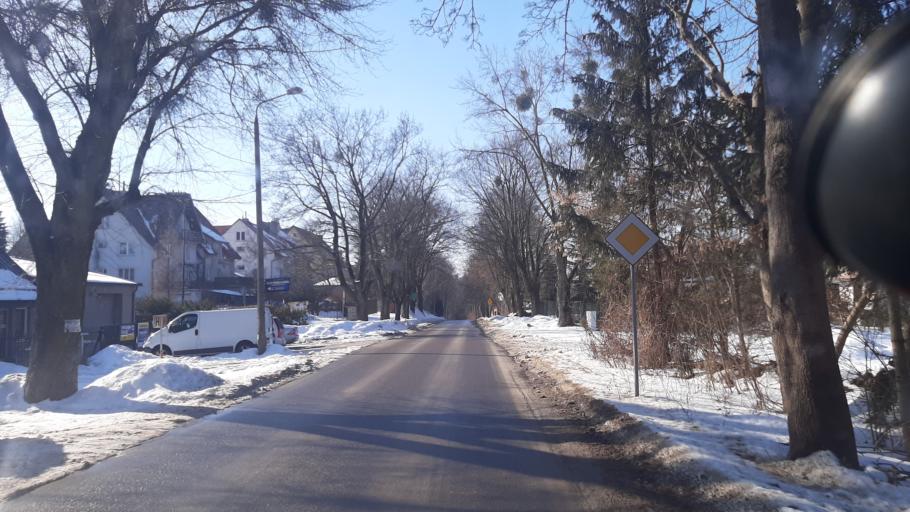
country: PL
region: Lublin Voivodeship
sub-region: Powiat pulawski
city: Naleczow
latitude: 51.2915
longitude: 22.2249
